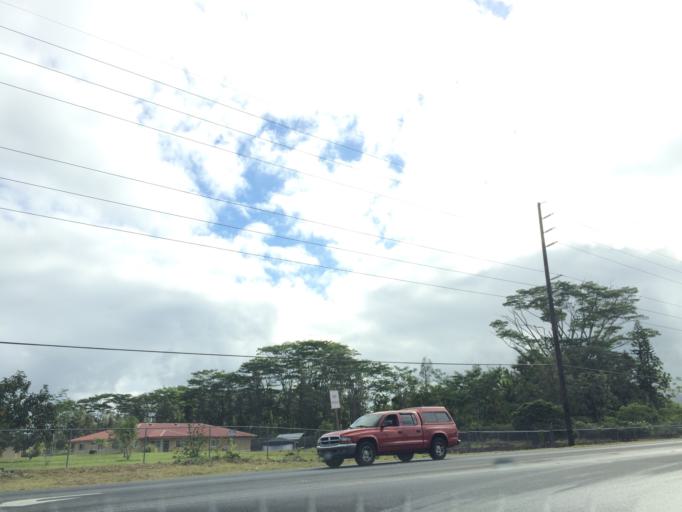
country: US
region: Hawaii
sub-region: Hawaii County
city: Orchidlands Estates
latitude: 19.5604
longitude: -154.9923
